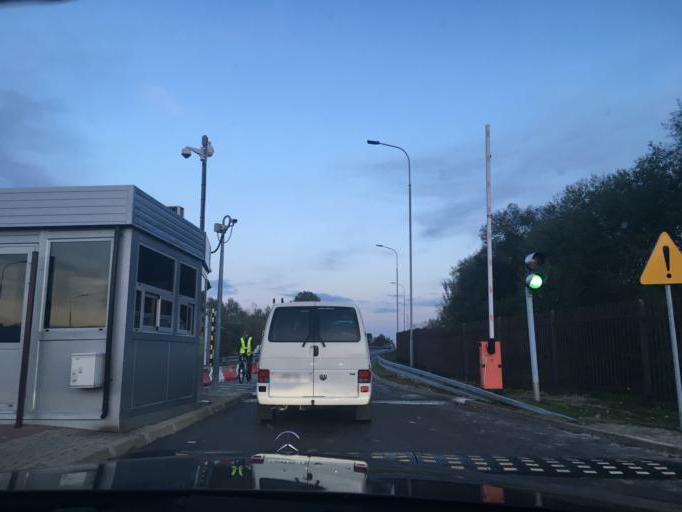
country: PL
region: Lublin Voivodeship
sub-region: Powiat bialski
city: Slawatycze
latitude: 51.7668
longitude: 23.5877
